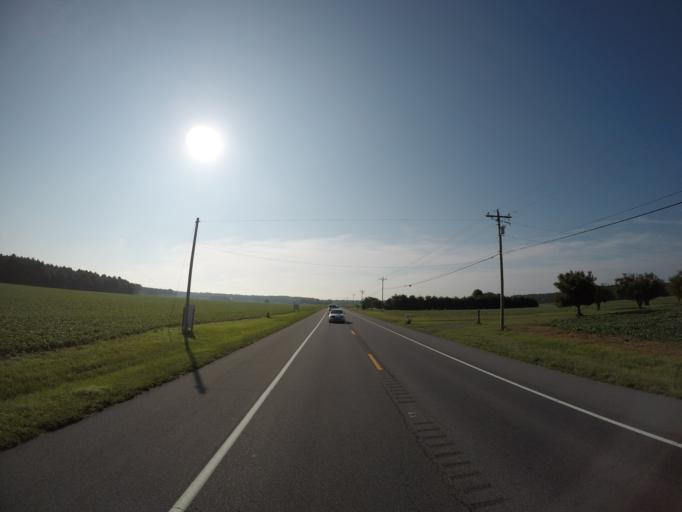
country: US
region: Delaware
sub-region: Sussex County
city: Georgetown
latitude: 38.6980
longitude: -75.4948
